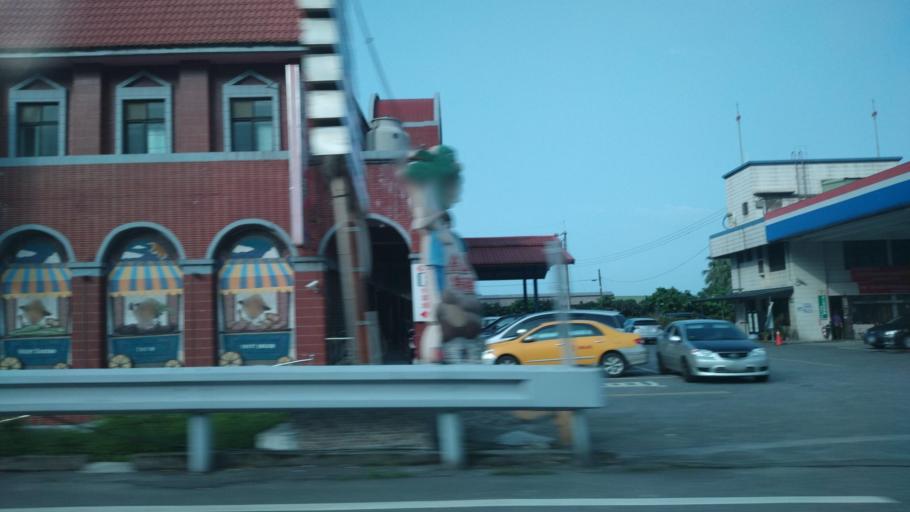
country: TW
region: Taiwan
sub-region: Keelung
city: Keelung
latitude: 25.2248
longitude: 121.6300
